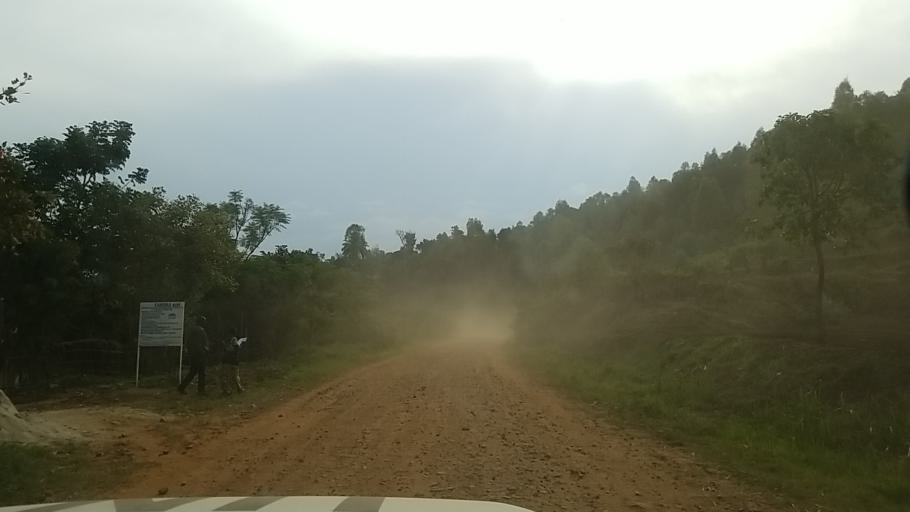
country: RW
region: Western Province
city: Cyangugu
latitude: -2.1052
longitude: 28.9092
